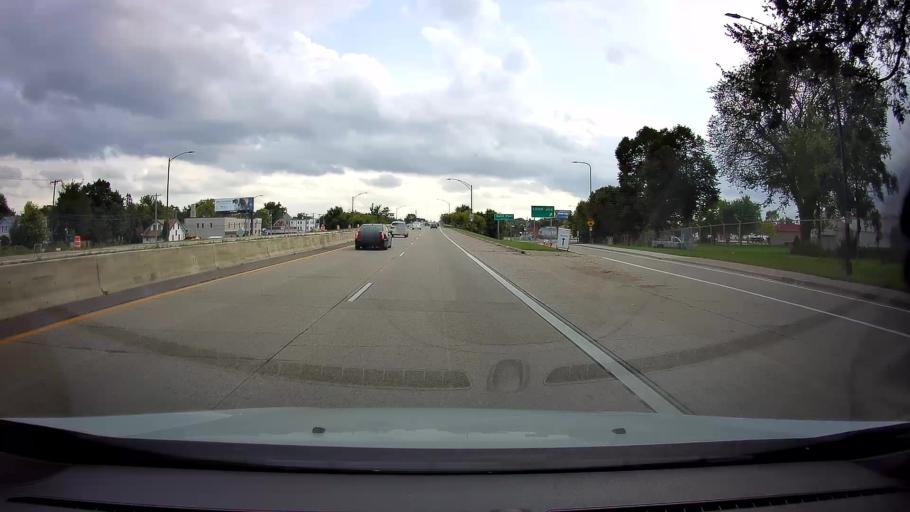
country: US
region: Minnesota
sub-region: Ramsey County
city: Falcon Heights
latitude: 44.9793
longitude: -93.1672
